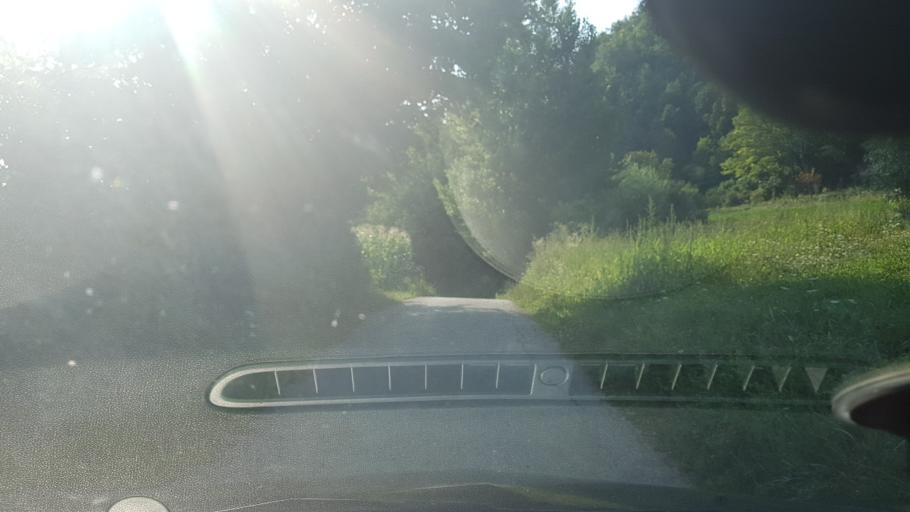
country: HR
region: Krapinsko-Zagorska
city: Radoboj
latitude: 46.1758
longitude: 15.9007
